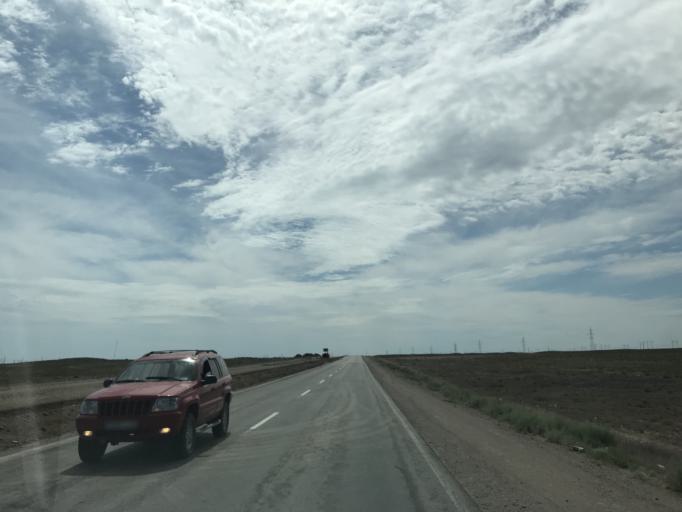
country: KZ
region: Almaty Oblysy
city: Ulken
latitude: 45.2288
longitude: 73.8463
